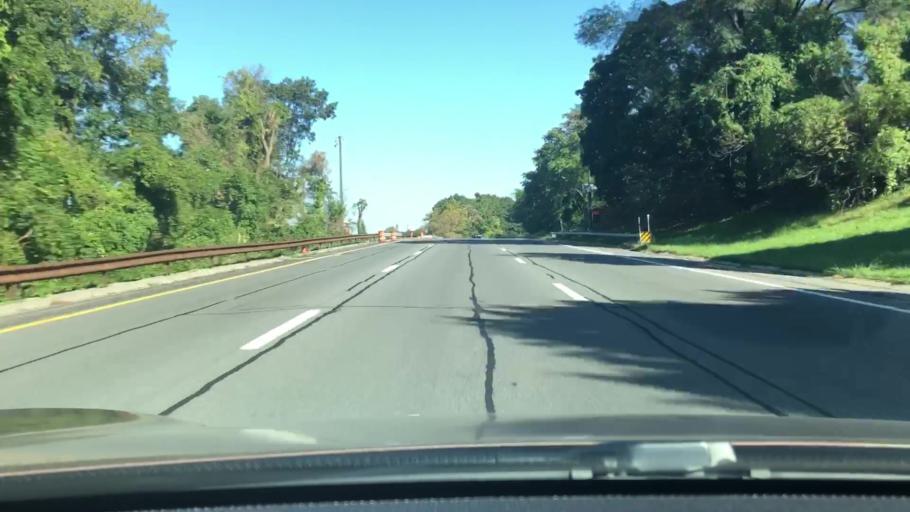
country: US
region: New York
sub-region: Westchester County
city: Tuckahoe
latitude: 40.9594
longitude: -73.8506
